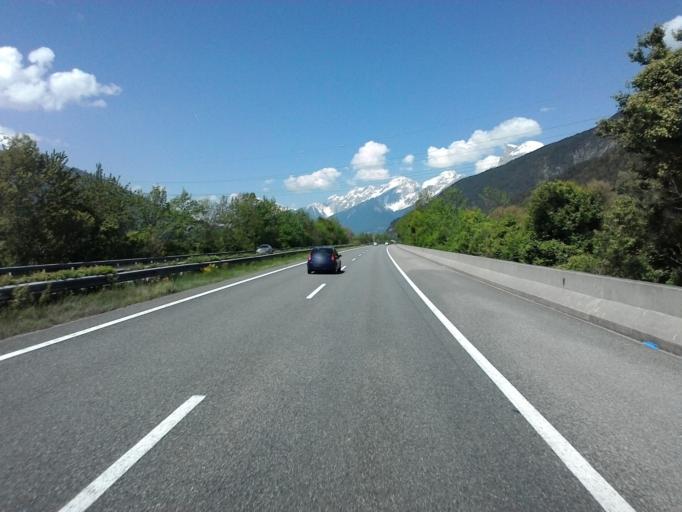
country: AT
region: Tyrol
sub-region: Politischer Bezirk Innsbruck Land
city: Ranggen
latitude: 47.2789
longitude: 11.2035
